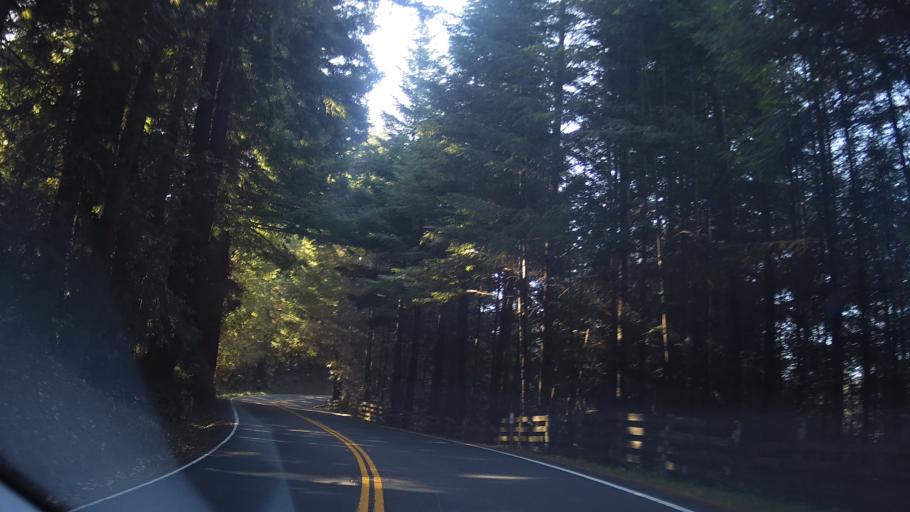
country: US
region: California
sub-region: Mendocino County
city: Fort Bragg
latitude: 39.3581
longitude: -123.6189
